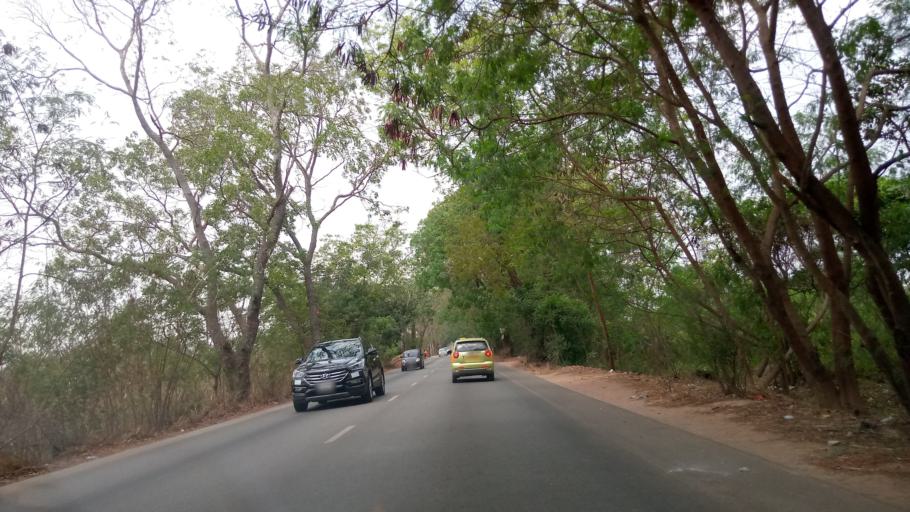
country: GH
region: Greater Accra
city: Dome
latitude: 5.6676
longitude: -0.2247
